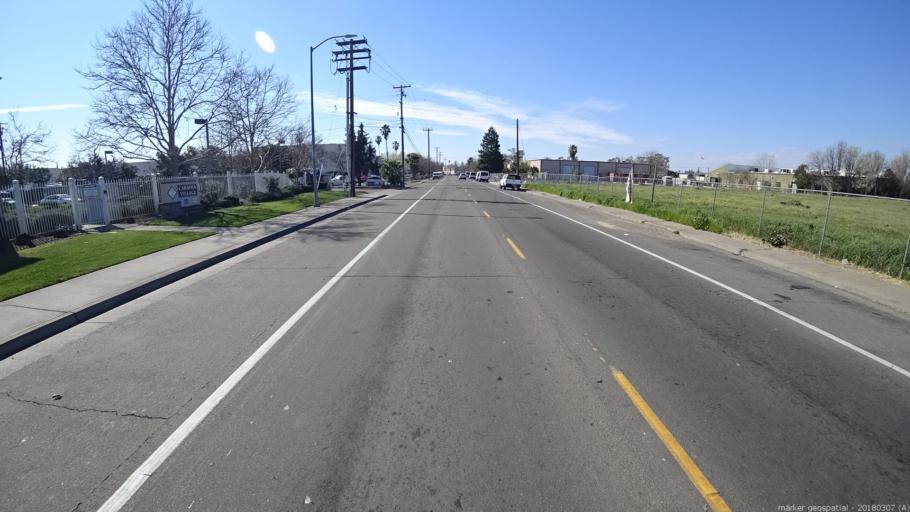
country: US
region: California
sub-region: Sacramento County
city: Parkway
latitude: 38.4924
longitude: -121.4384
